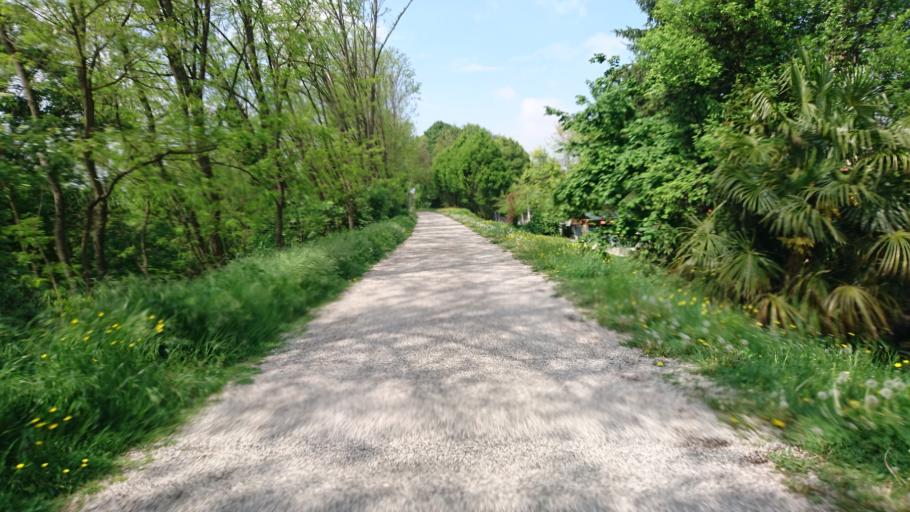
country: IT
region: Veneto
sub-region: Provincia di Padova
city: Vigodarzere
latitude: 45.4535
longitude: 11.8814
